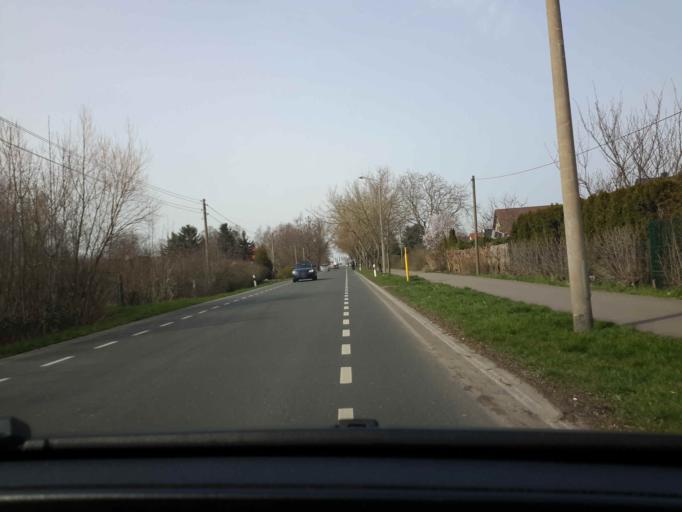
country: DE
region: Saxony
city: Rackwitz
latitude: 51.4012
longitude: 12.3683
